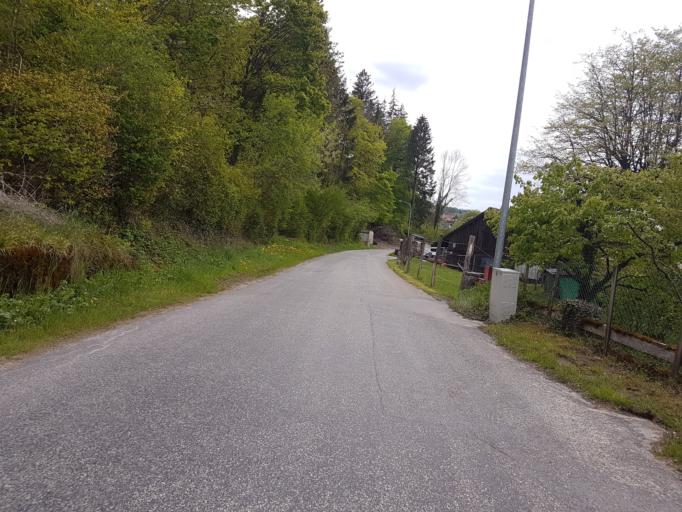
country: CH
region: Bern
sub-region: Seeland District
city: Leuzigen
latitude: 47.1736
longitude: 7.4682
